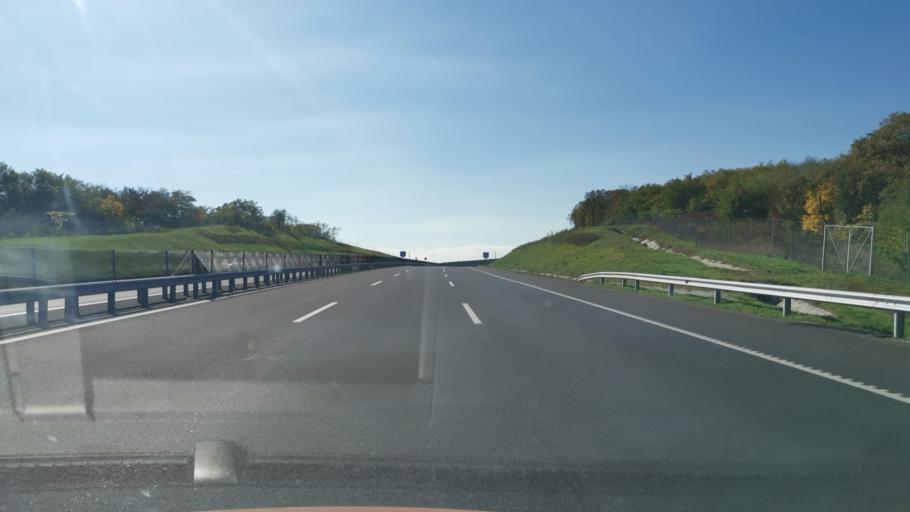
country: HU
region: Borsod-Abauj-Zemplen
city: Szikszo
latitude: 48.2212
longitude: 20.9381
